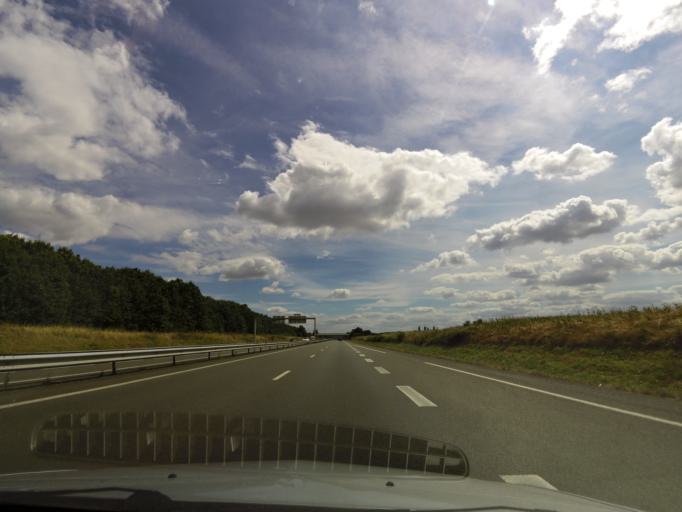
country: FR
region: Pays de la Loire
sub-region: Departement de la Vendee
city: Bouffere
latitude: 46.9594
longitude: -1.3573
